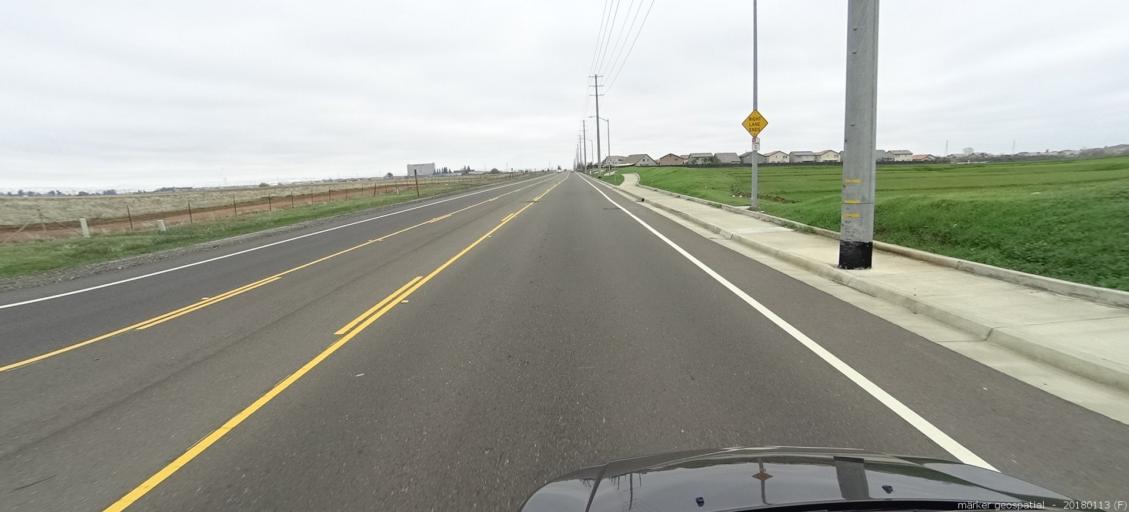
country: US
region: California
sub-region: Sacramento County
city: Gold River
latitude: 38.5592
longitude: -121.2229
